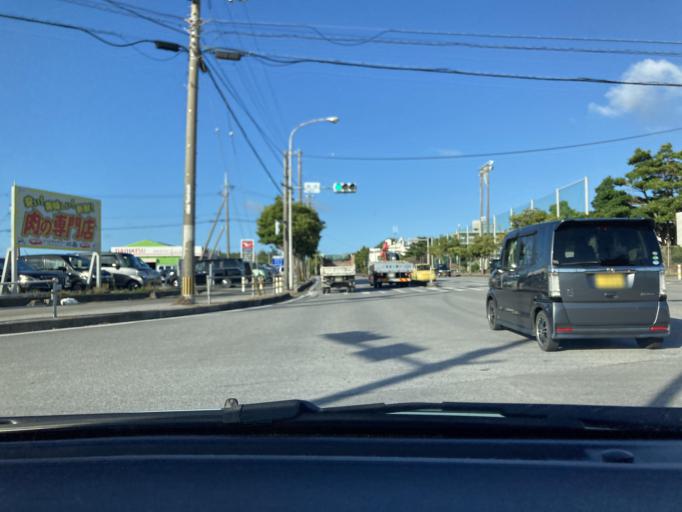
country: JP
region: Okinawa
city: Tomigusuku
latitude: 26.1722
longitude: 127.7106
